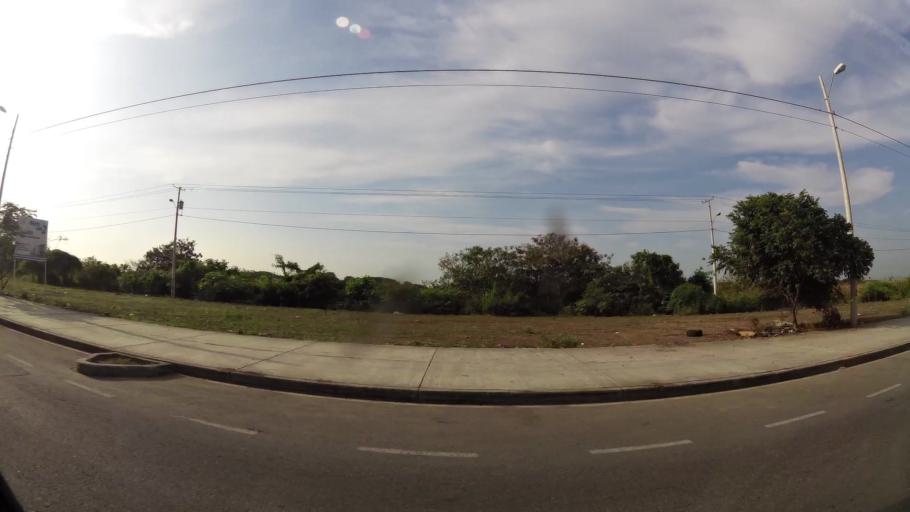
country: EC
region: Guayas
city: Eloy Alfaro
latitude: -2.0648
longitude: -79.8904
